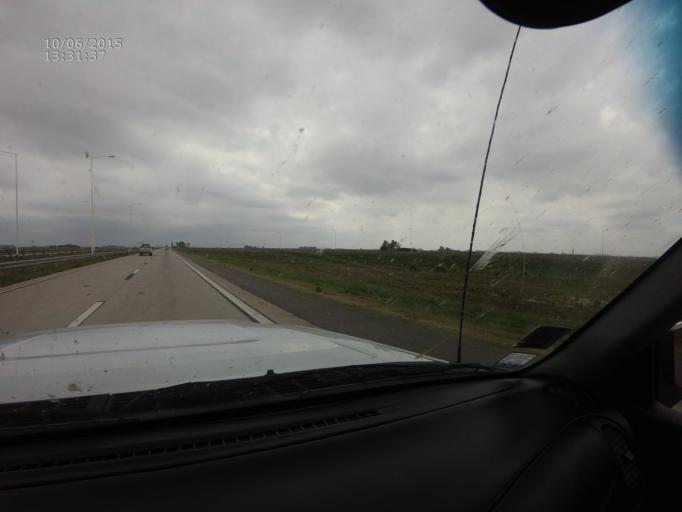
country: AR
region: Cordoba
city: Leones
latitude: -32.6302
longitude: -62.2896
